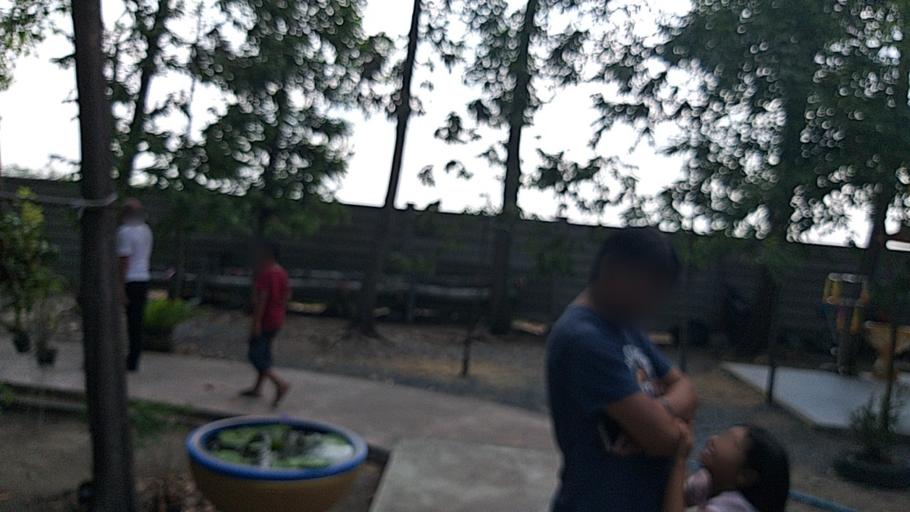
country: TH
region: Pathum Thani
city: Nong Suea
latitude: 14.1875
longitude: 100.8364
